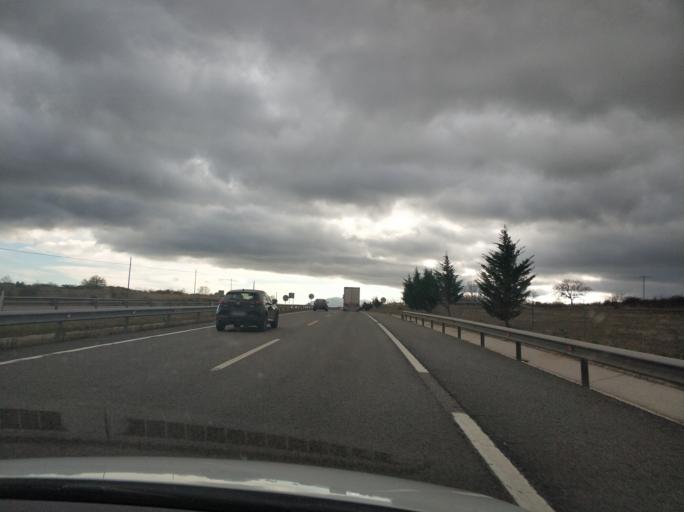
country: ES
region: Madrid
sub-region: Provincia de Madrid
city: Horcajo de la Sierra
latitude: 41.0562
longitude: -3.6137
